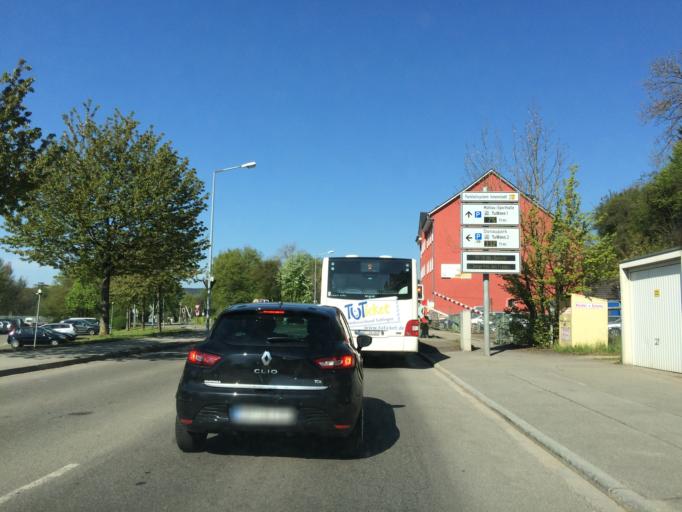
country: DE
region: Baden-Wuerttemberg
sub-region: Freiburg Region
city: Tuttlingen
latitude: 47.9861
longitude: 8.8158
